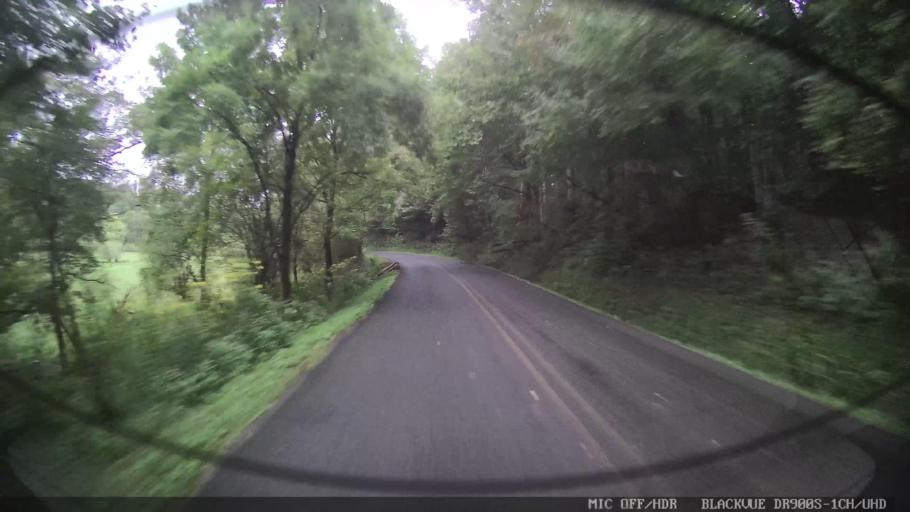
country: US
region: Georgia
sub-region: Gilmer County
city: Ellijay
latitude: 34.7651
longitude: -84.5320
